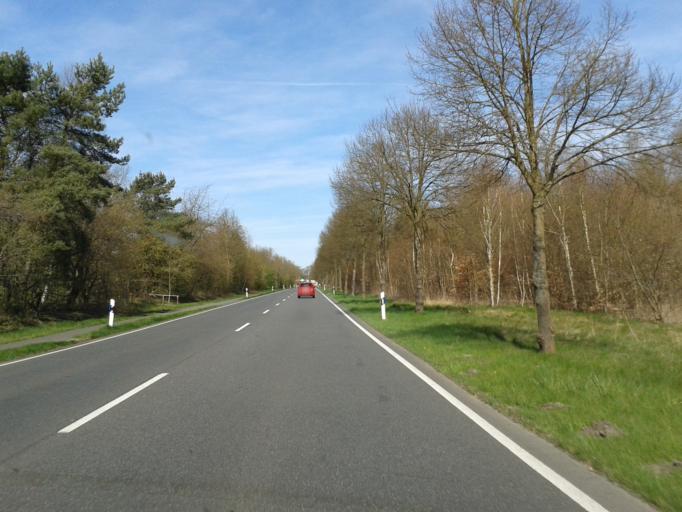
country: DE
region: Lower Saxony
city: Munster
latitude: 52.9767
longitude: 10.0999
